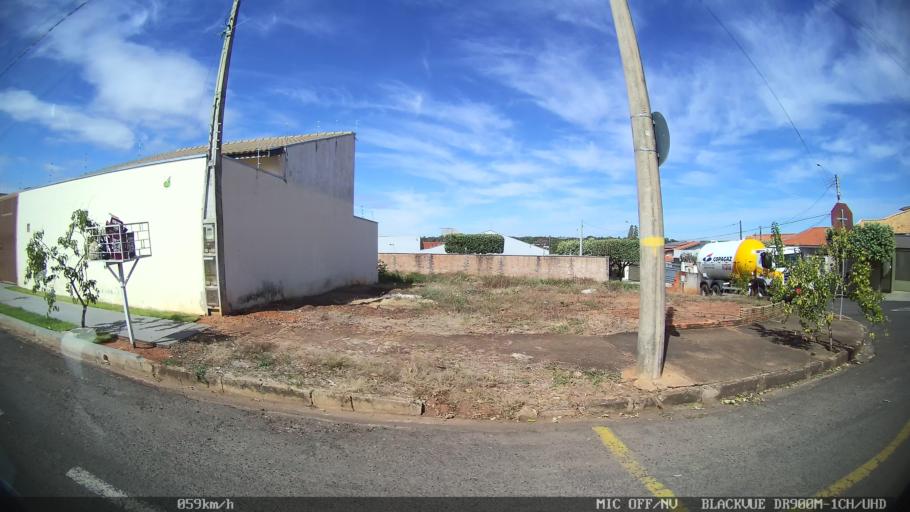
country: BR
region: Sao Paulo
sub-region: Sao Jose Do Rio Preto
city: Sao Jose do Rio Preto
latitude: -20.8400
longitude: -49.3583
